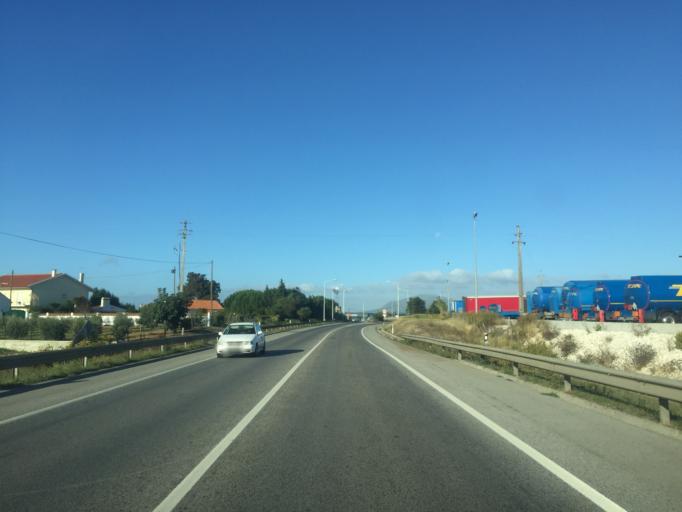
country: PT
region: Lisbon
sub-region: Azambuja
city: Aveiras de Cima
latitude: 39.1447
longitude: -8.8987
